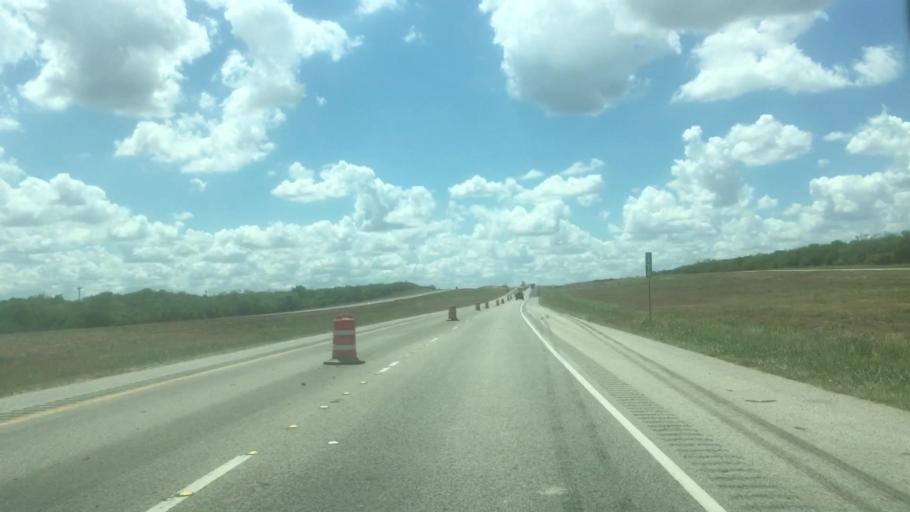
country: US
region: Texas
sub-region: Caldwell County
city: Lockhart
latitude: 29.8277
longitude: -97.7448
